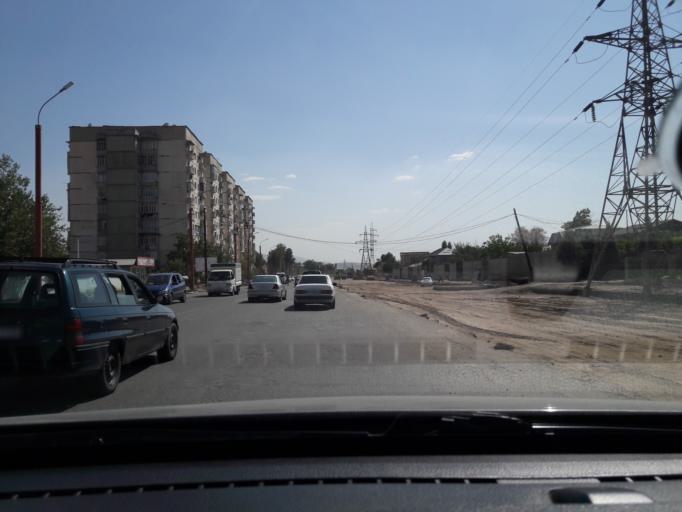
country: TJ
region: Dushanbe
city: Dushanbe
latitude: 38.5353
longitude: 68.7399
